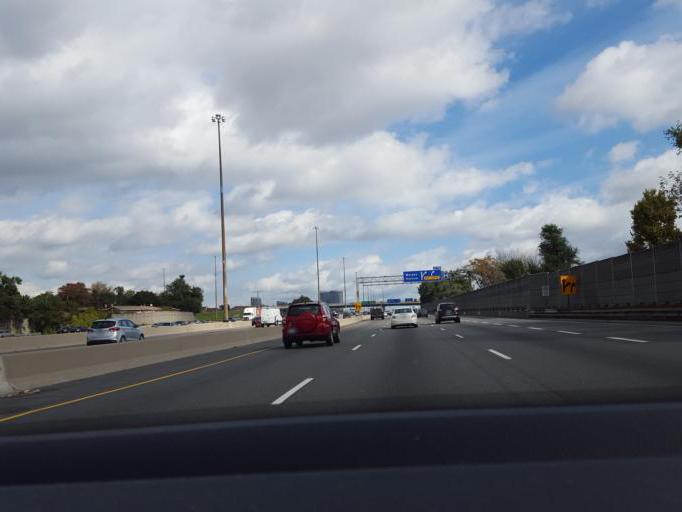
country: CA
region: Ontario
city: Scarborough
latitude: 43.7687
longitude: -79.3101
